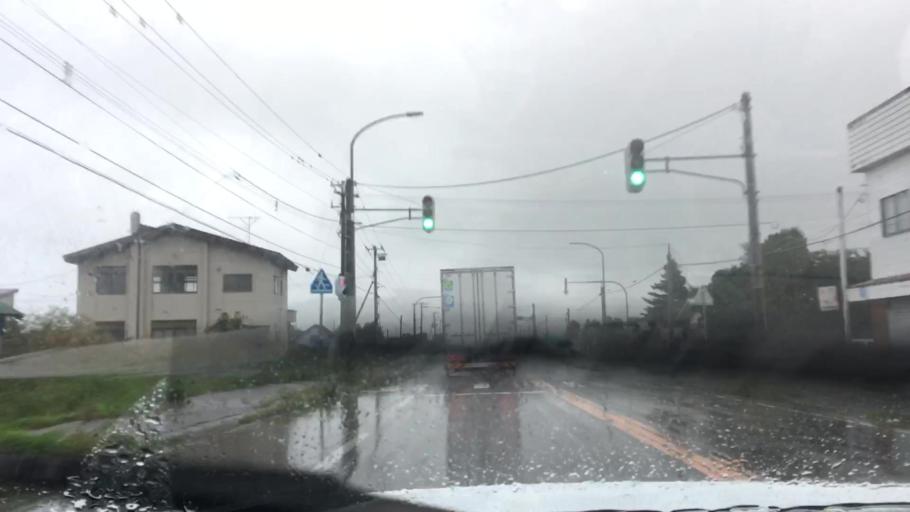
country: JP
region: Hokkaido
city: Niseko Town
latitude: 42.4777
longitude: 140.3484
